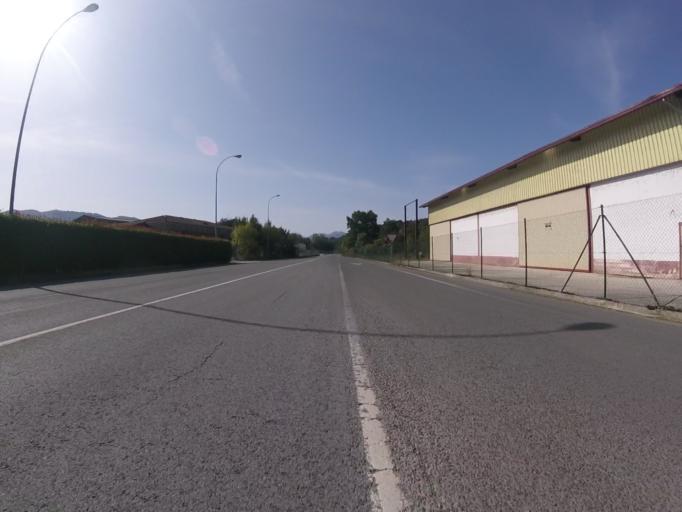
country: ES
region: Navarre
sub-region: Provincia de Navarra
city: Zugarramurdi
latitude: 43.1803
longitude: -1.4907
